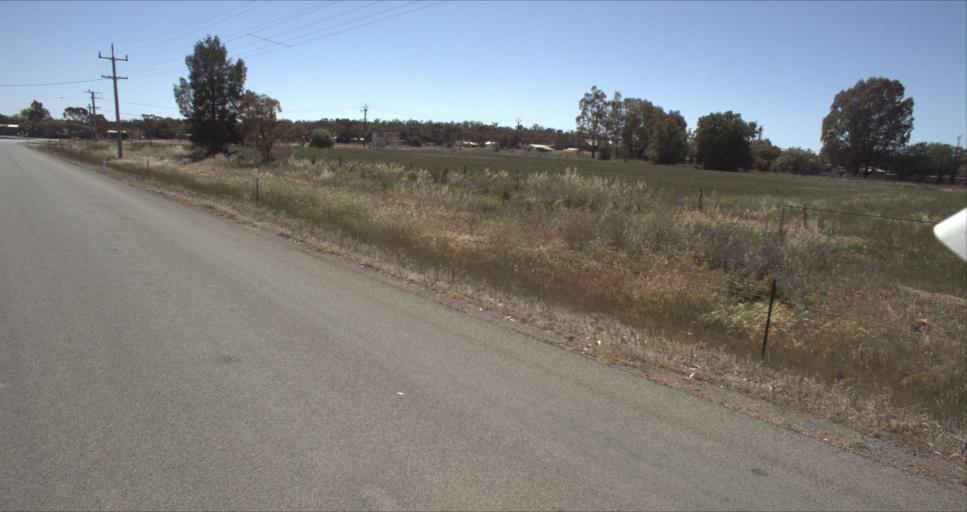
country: AU
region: New South Wales
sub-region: Leeton
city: Leeton
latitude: -34.4289
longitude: 146.3000
